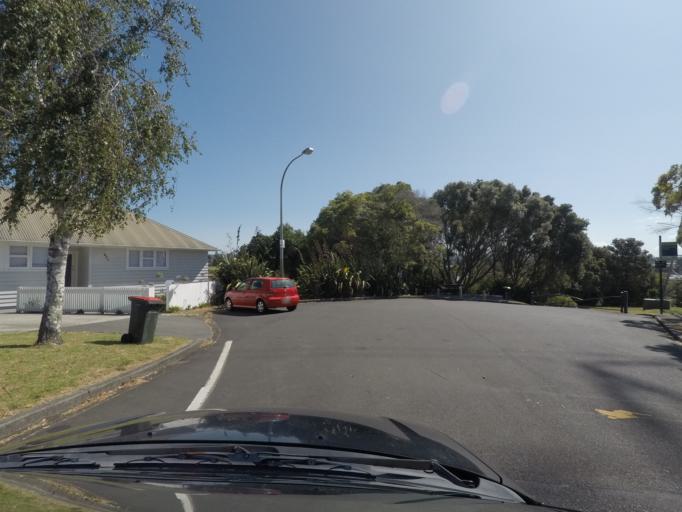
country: NZ
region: Auckland
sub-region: Auckland
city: Rosebank
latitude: -36.8892
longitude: 174.6731
